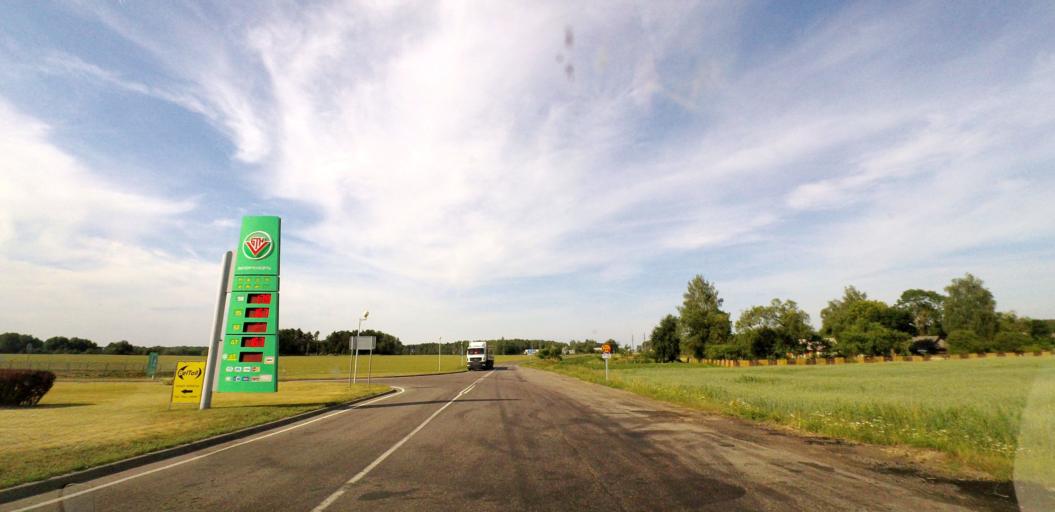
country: BY
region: Grodnenskaya
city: Lida
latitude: 53.8301
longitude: 25.3641
